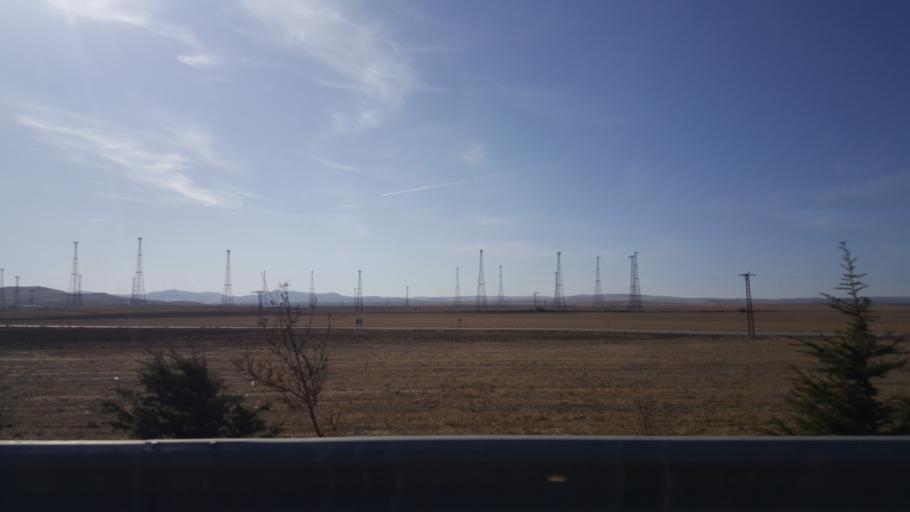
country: TR
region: Ankara
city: Yenice
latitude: 39.4084
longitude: 32.8705
